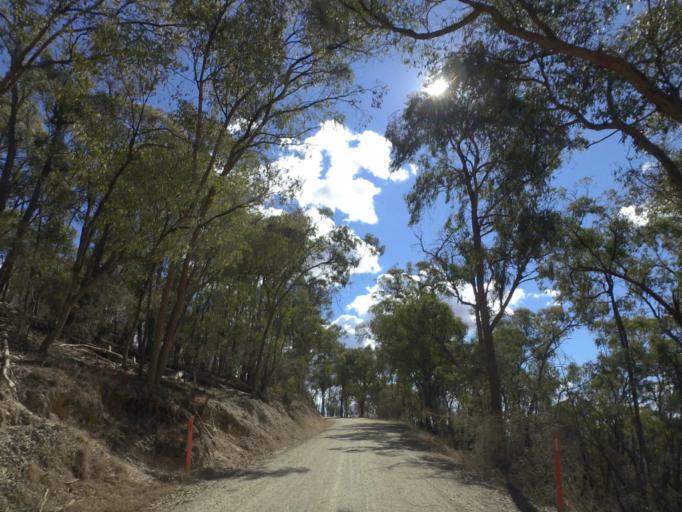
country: AU
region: Victoria
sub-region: Murrindindi
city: Alexandra
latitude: -37.3228
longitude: 145.8095
